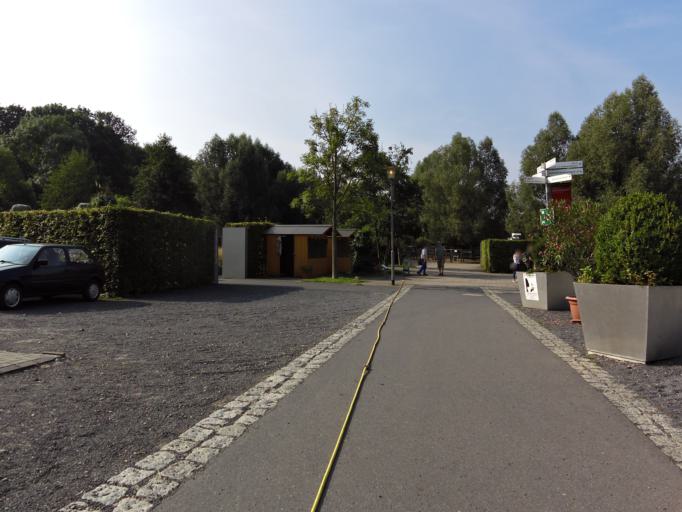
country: DE
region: Saxony
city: Oschatz
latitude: 51.2932
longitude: 13.1101
